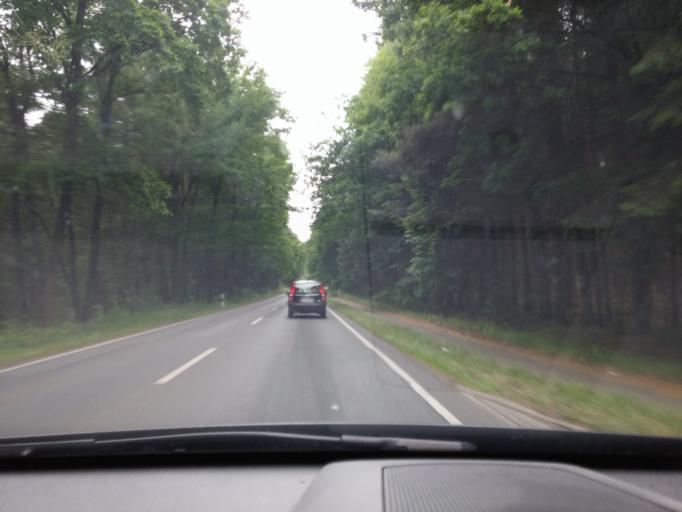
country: DE
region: Lower Saxony
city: Harmstorf
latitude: 53.3267
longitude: 9.9760
